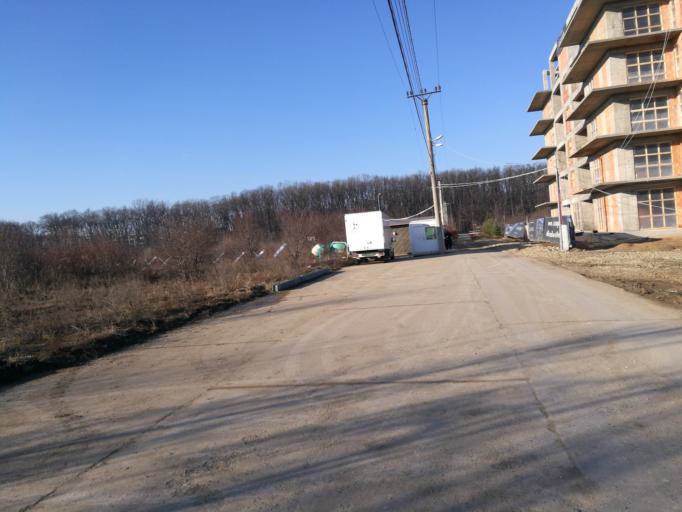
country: RO
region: Ilfov
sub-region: Comuna Otopeni
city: Otopeni
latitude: 44.5107
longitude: 26.0758
